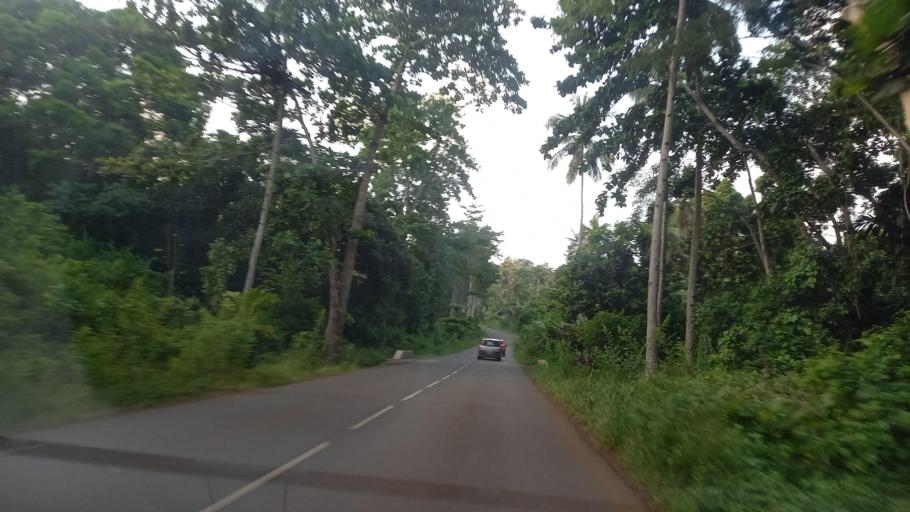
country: YT
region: M'Tsangamouji
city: M'Tsangamouji
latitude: -12.7566
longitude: 45.0956
